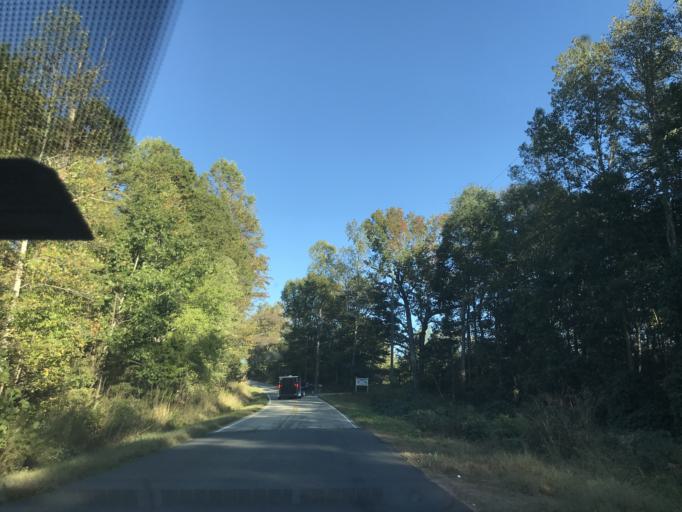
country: US
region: South Carolina
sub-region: Spartanburg County
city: Mayo
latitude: 35.1195
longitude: -81.8045
